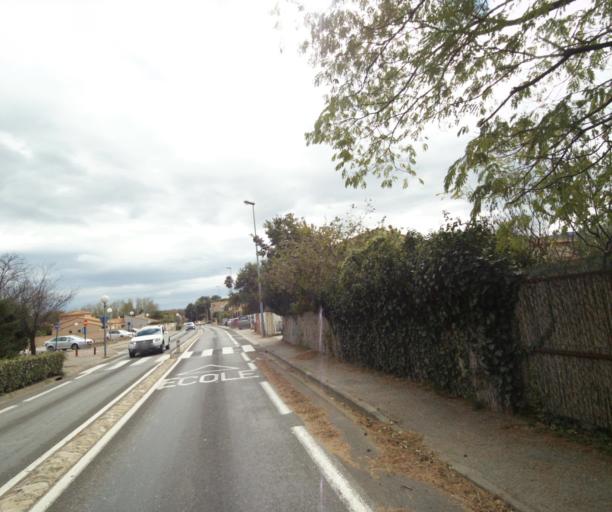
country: FR
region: Languedoc-Roussillon
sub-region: Departement des Pyrenees-Orientales
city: Argelers
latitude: 42.5530
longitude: 3.0275
